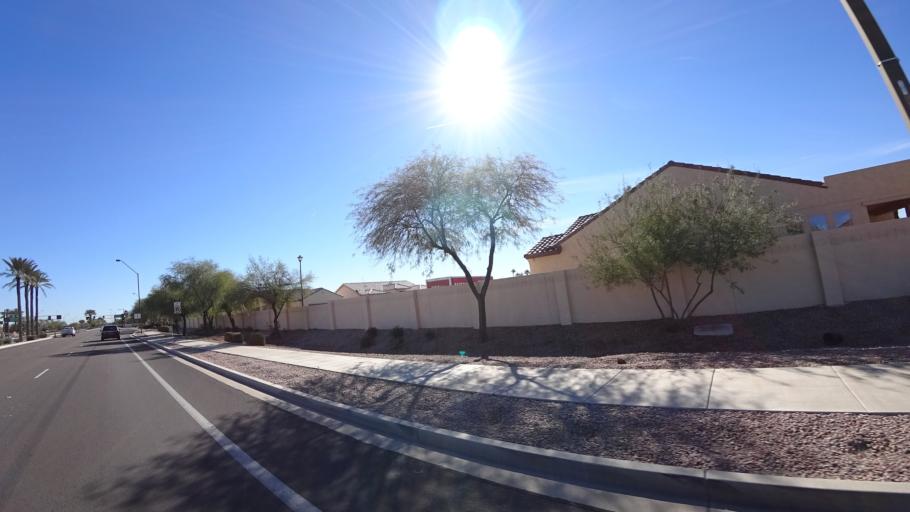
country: US
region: Arizona
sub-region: Maricopa County
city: Litchfield Park
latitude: 33.4936
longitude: -112.4033
